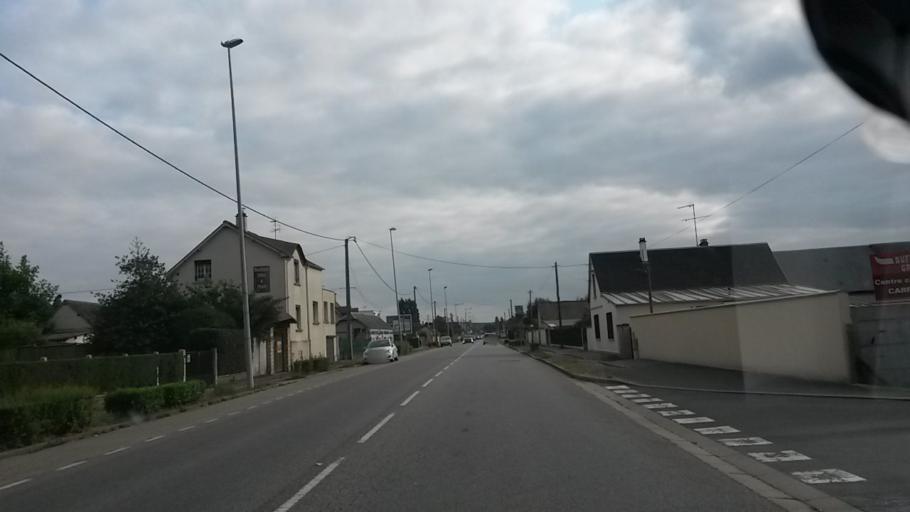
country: FR
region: Haute-Normandie
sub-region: Departement de l'Eure
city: Gravigny
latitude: 49.0526
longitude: 1.1659
